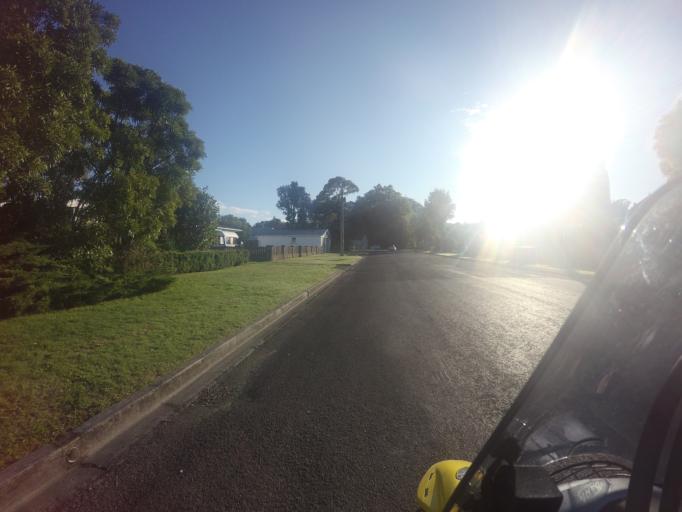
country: NZ
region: Gisborne
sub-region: Gisborne District
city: Gisborne
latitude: -38.6657
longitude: 178.0490
